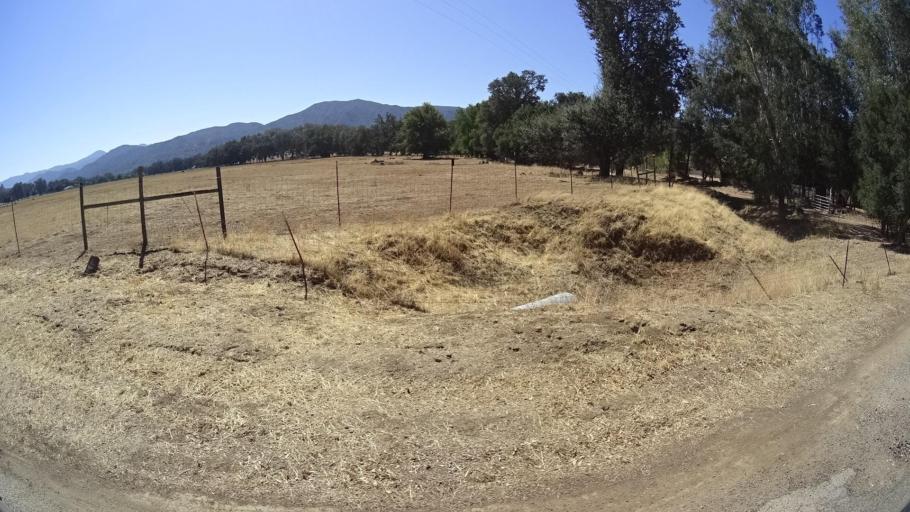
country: US
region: California
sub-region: San Luis Obispo County
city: Lake Nacimiento
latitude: 35.8147
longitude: -121.0913
